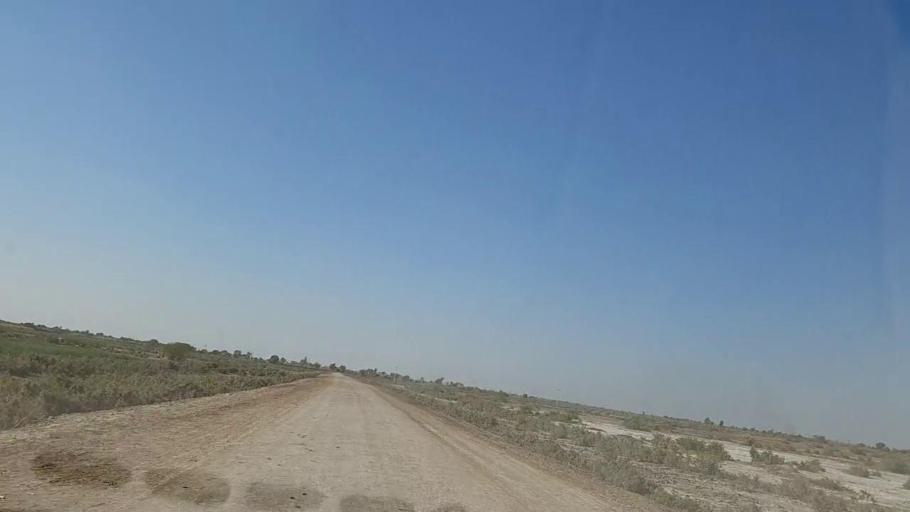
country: PK
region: Sindh
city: Digri
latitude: 25.1865
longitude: 69.0016
